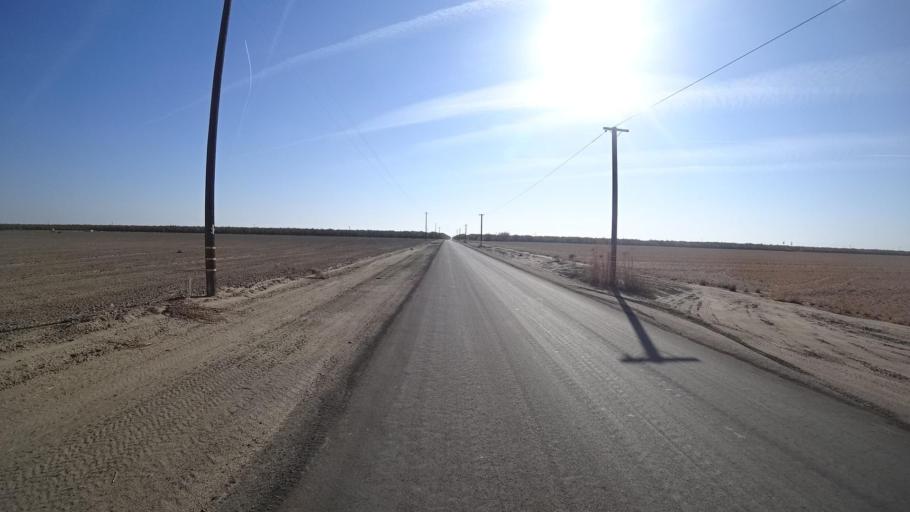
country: US
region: California
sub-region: Kern County
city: Wasco
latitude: 35.6627
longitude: -119.3840
